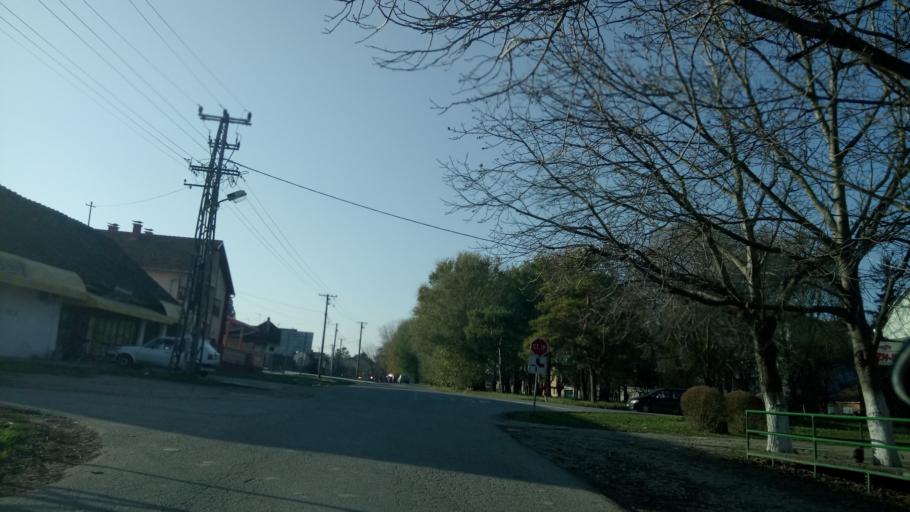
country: RS
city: Beska
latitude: 45.1245
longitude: 20.0679
